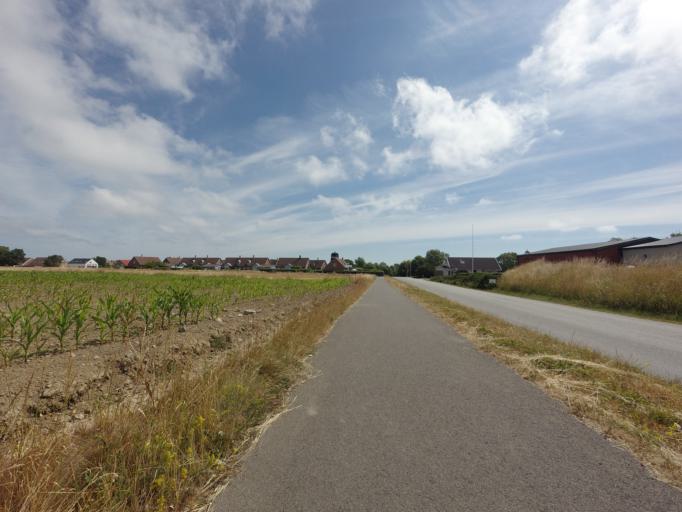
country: SE
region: Skane
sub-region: Simrishamns Kommun
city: Simrishamn
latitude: 55.5123
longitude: 14.3405
